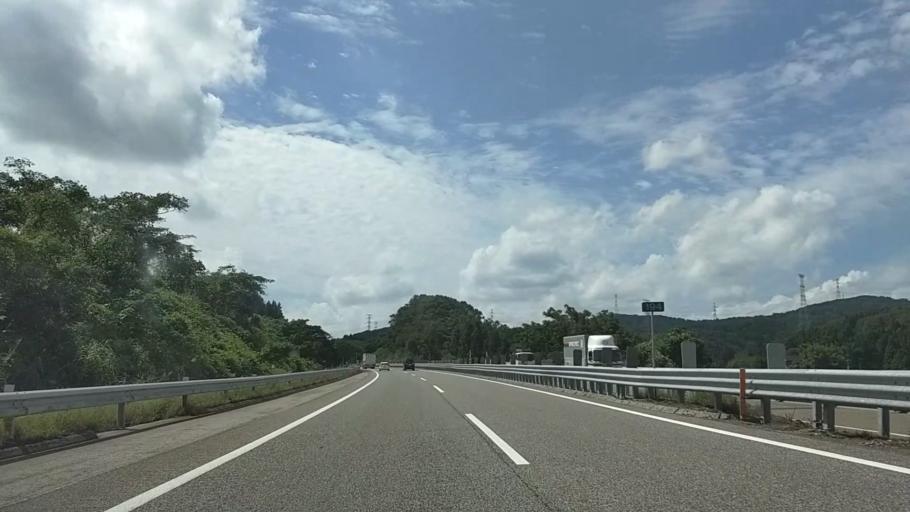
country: JP
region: Toyama
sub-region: Oyabe Shi
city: Oyabe
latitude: 36.6139
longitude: 136.8158
